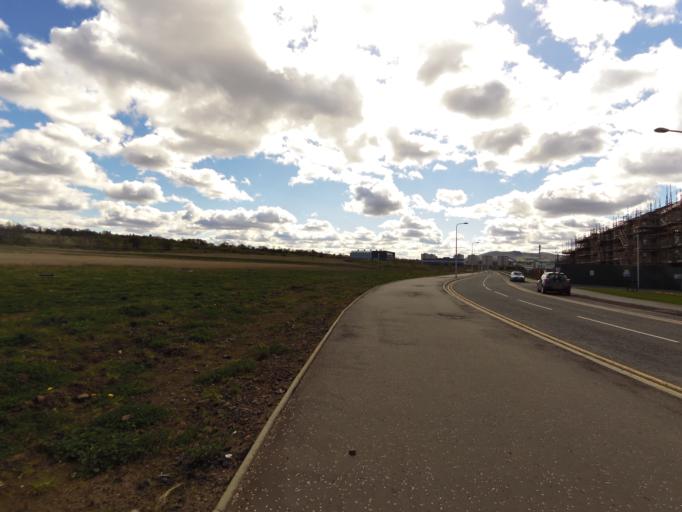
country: GB
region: Scotland
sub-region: West Lothian
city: Seafield
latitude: 55.9252
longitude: -3.1238
